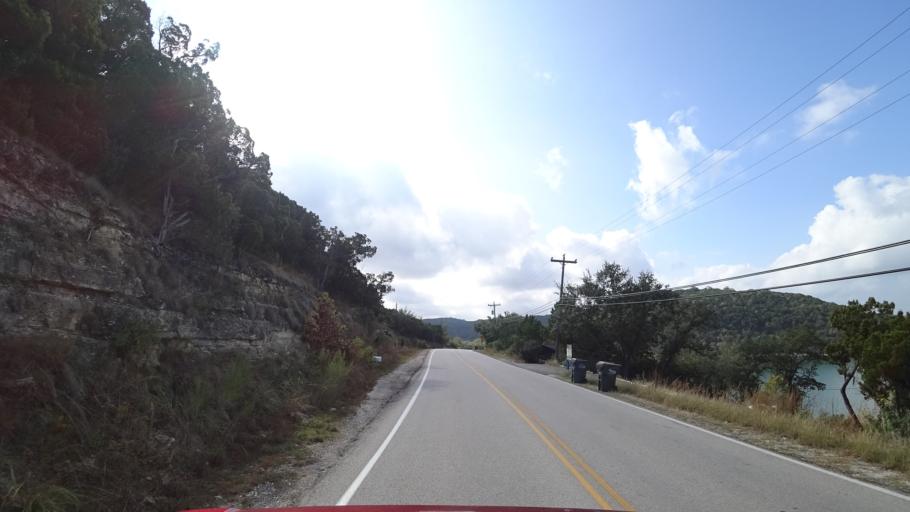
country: US
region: Texas
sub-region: Travis County
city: Hudson Bend
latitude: 30.4318
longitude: -97.8737
